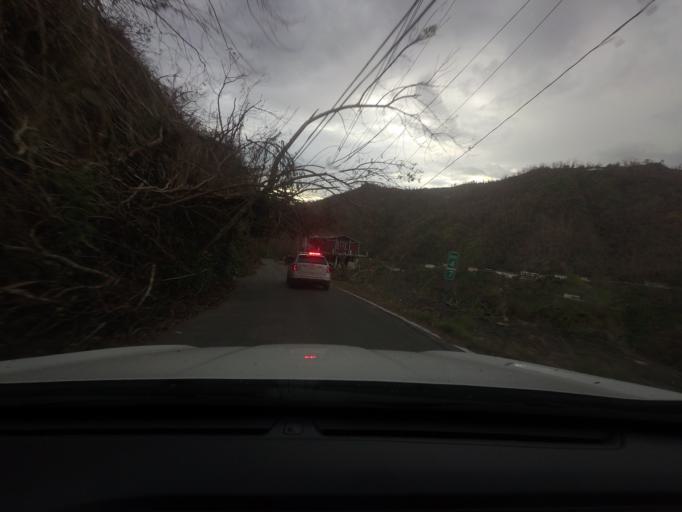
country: PR
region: Ciales
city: Ciales
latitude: 18.2901
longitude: -66.4853
